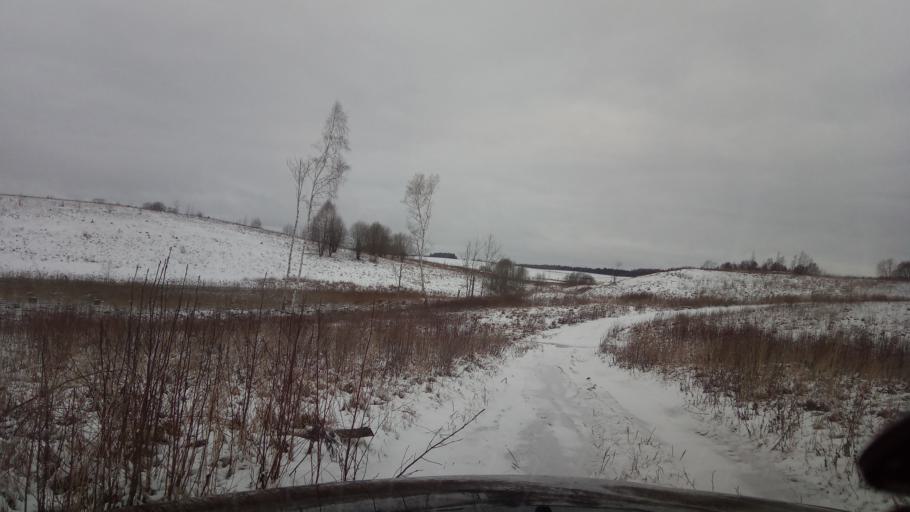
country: LT
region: Utenos apskritis
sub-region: Utena
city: Utena
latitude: 55.6084
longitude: 25.8672
